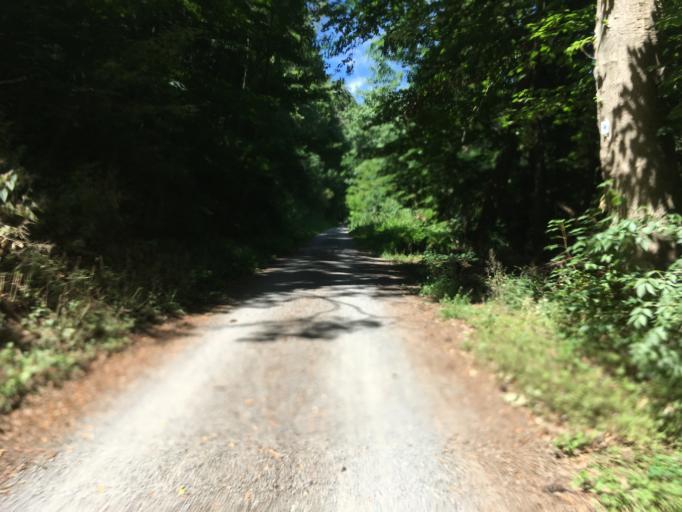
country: DE
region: Baden-Wuerttemberg
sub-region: Regierungsbezirk Stuttgart
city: Vaihingen an der Enz
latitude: 48.9156
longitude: 8.9591
